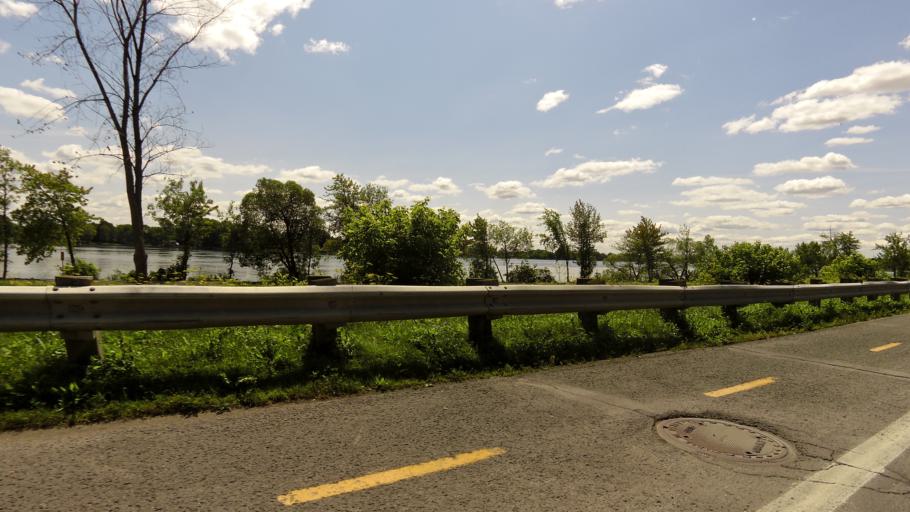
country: CA
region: Quebec
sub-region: Monteregie
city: Saint-Jean-sur-Richelieu
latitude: 45.3459
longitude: -73.2653
